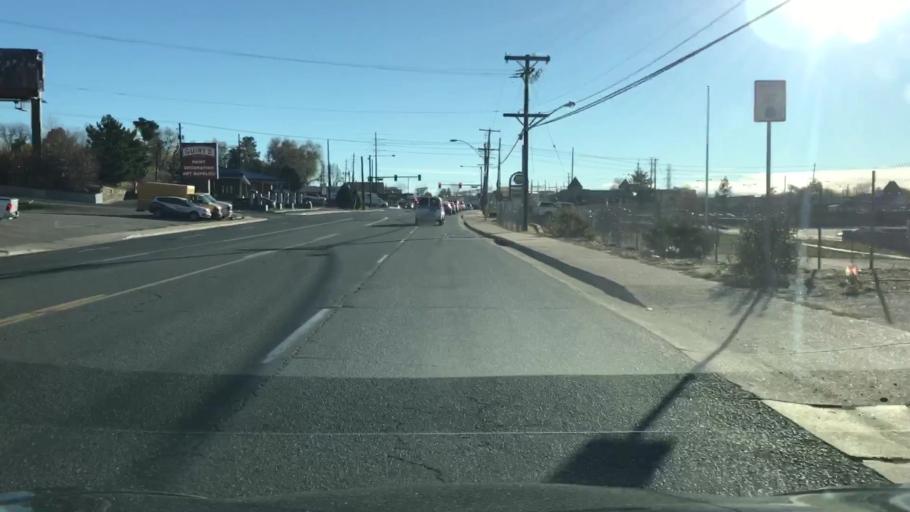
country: US
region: Colorado
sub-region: Arapahoe County
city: Glendale
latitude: 39.7076
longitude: -104.9245
